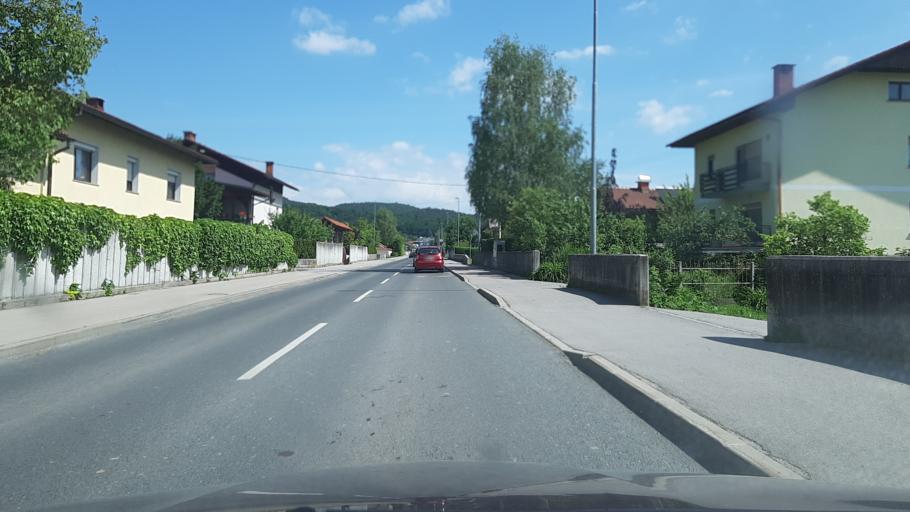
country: SI
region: Brezovica
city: Vnanje Gorice
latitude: 46.0144
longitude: 14.4138
